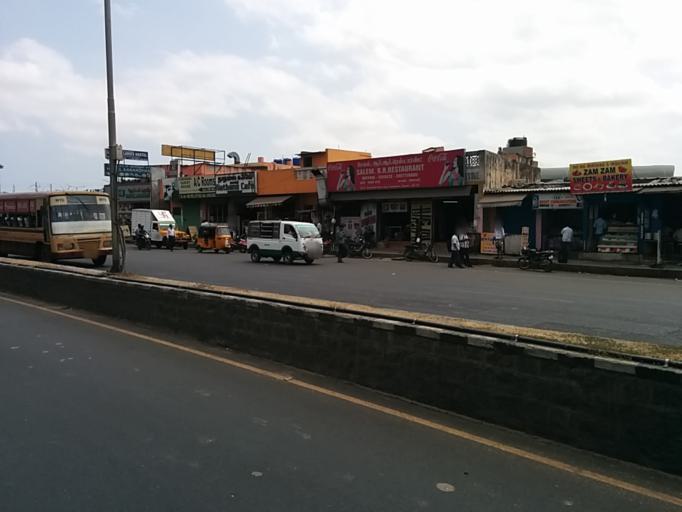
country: IN
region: Tamil Nadu
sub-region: Chennai
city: Chetput
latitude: 13.0706
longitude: 80.2041
